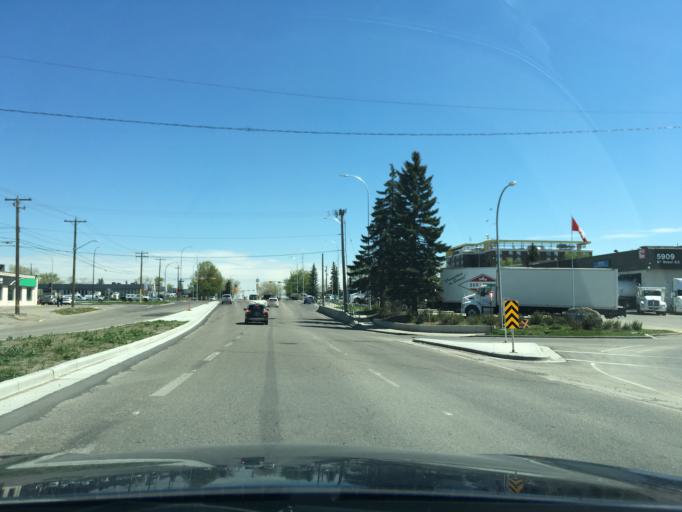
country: CA
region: Alberta
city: Calgary
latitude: 51.0014
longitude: -114.0514
